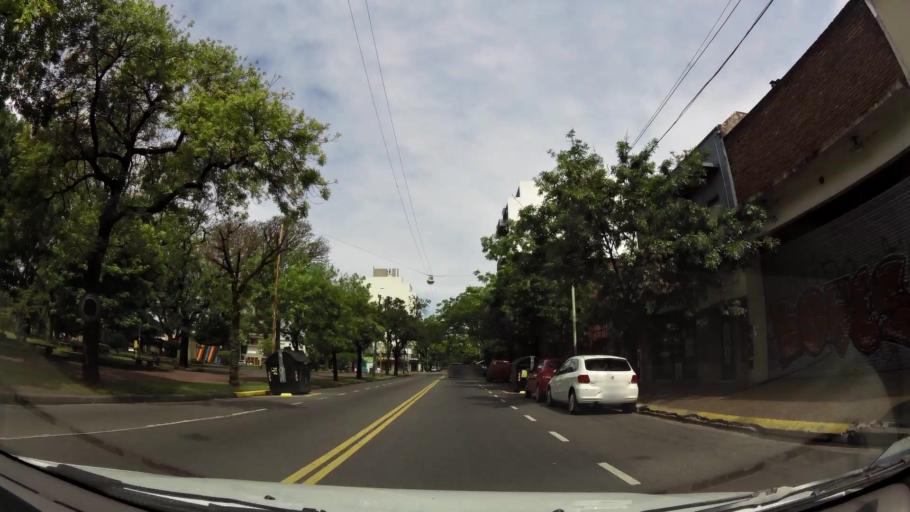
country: AR
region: Buenos Aires F.D.
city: Villa Santa Rita
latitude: -34.6263
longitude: -58.5091
